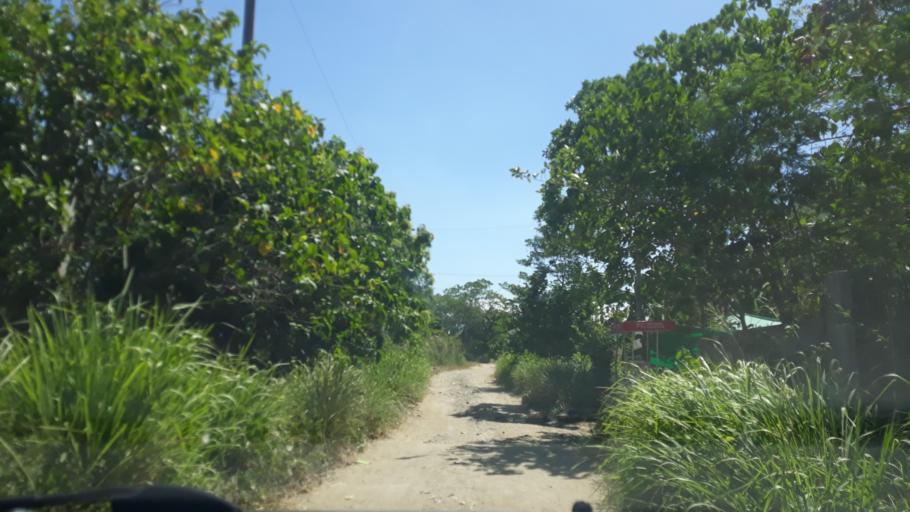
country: PH
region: Calabarzon
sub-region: Province of Cavite
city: Manggahan
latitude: 14.3018
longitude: 120.9143
